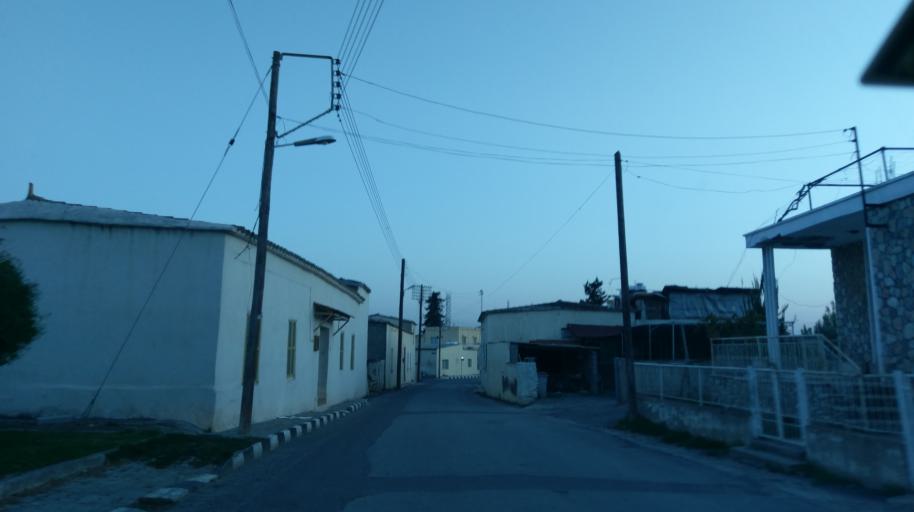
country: CY
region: Ammochostos
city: Trikomo
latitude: 35.2869
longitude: 33.8923
